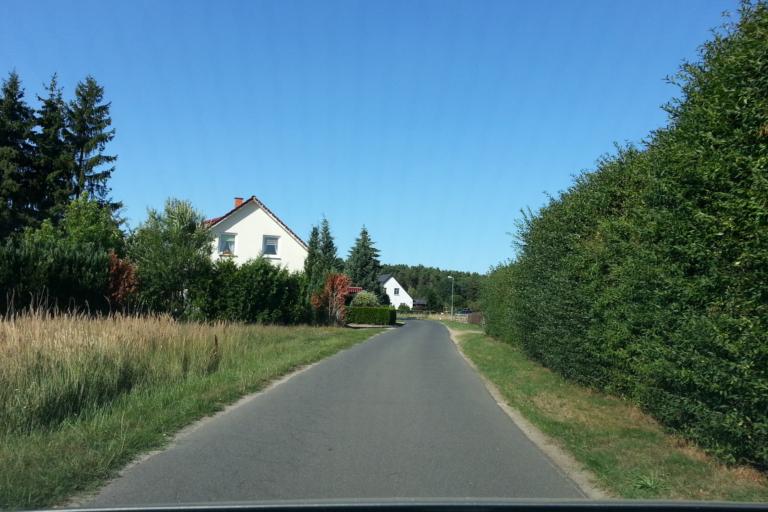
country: DE
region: Mecklenburg-Vorpommern
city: Eggesin
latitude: 53.6830
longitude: 14.0389
